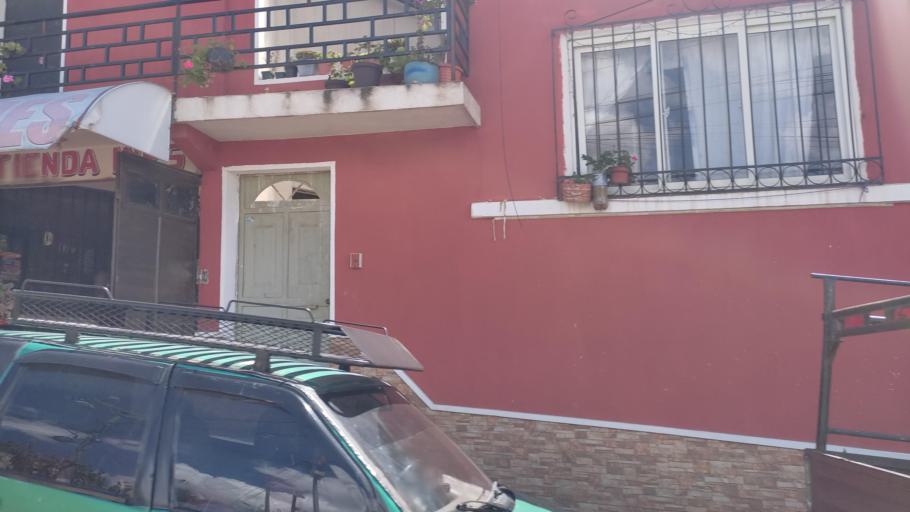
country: GT
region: Quetzaltenango
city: Quetzaltenango
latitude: 14.8578
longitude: -91.5267
